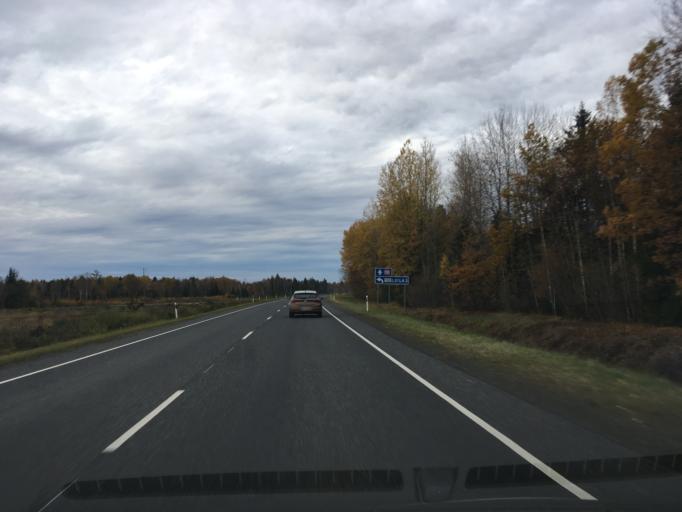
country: EE
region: Harju
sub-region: Nissi vald
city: Turba
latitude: 58.9390
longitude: 24.0907
